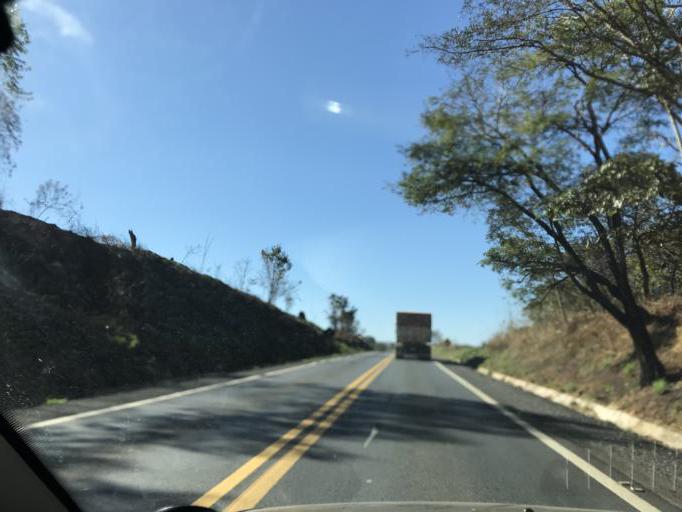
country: BR
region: Minas Gerais
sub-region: Bambui
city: Bambui
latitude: -19.8687
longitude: -45.9862
